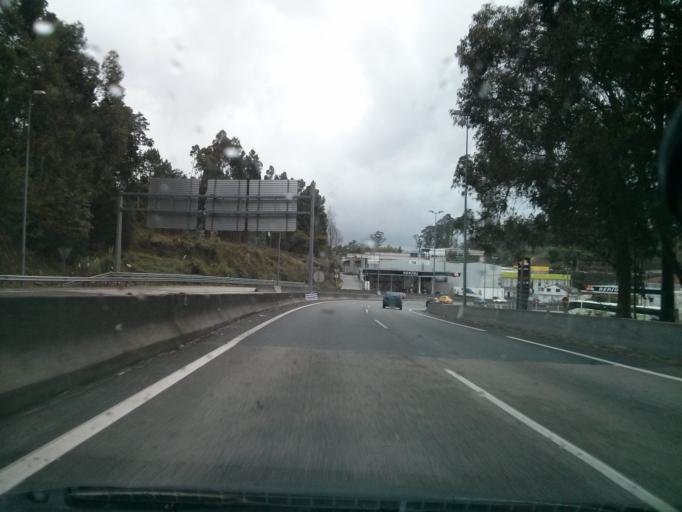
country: ES
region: Galicia
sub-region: Provincia de Pontevedra
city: Vigo
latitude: 42.2119
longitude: -8.6667
